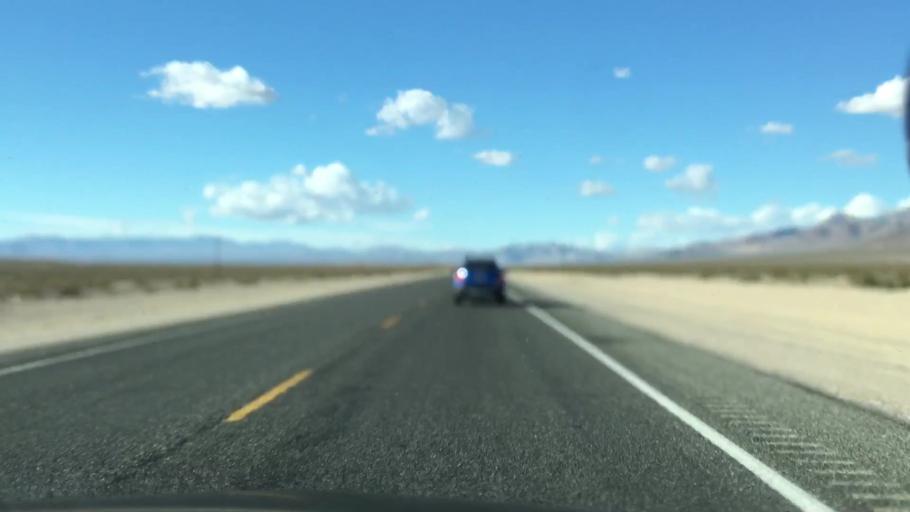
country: US
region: Nevada
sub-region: Nye County
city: Beatty
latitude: 36.7308
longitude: -116.6324
